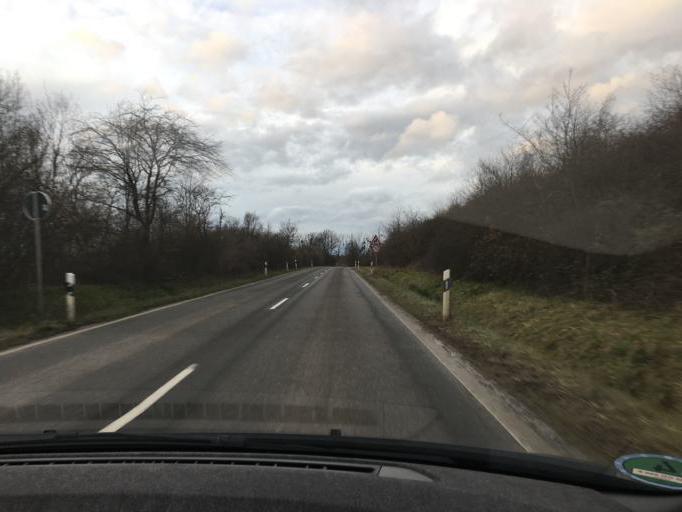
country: DE
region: North Rhine-Westphalia
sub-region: Regierungsbezirk Koln
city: Bad Munstereifel
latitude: 50.6104
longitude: 6.7337
